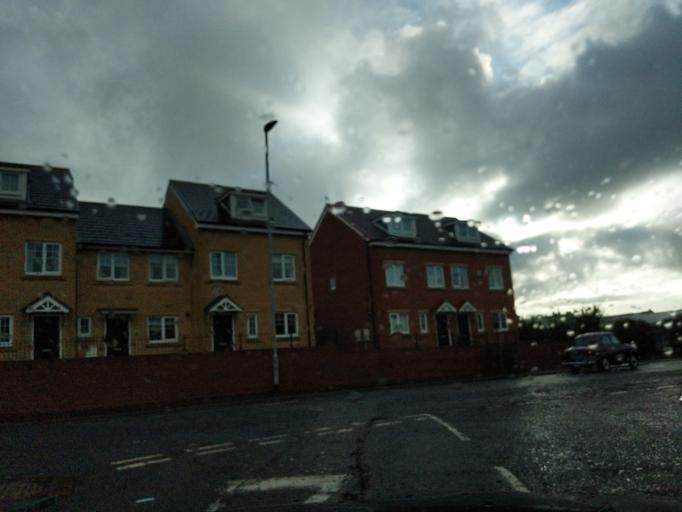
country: GB
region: England
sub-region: Northumberland
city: Blyth
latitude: 55.1234
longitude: -1.5061
